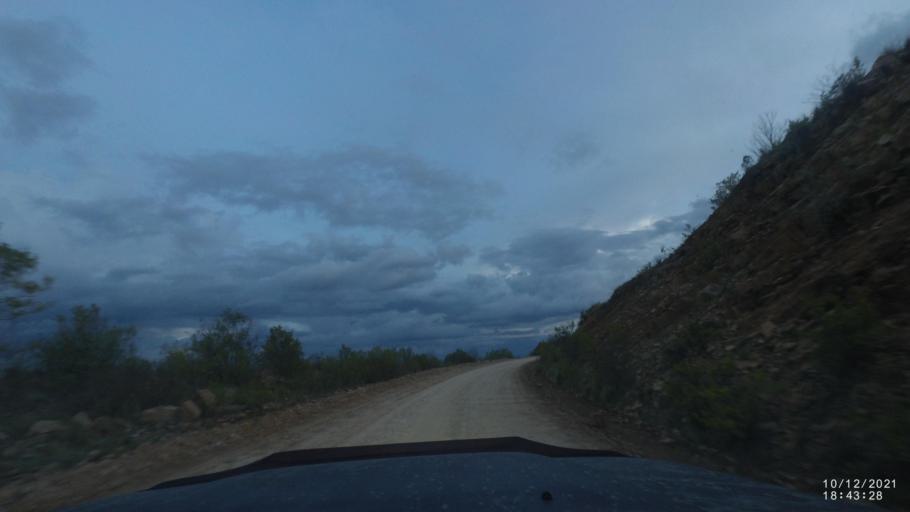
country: BO
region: Cochabamba
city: Tarata
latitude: -17.8761
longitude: -65.9791
